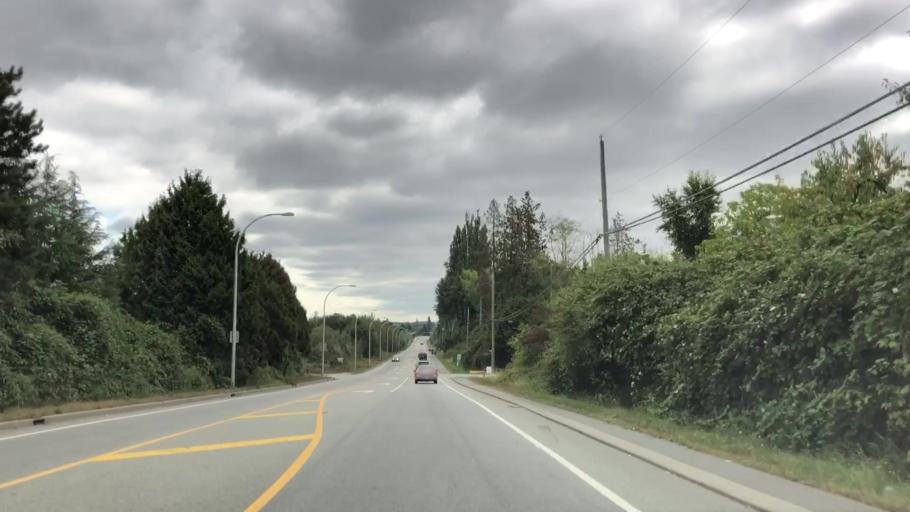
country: CA
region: British Columbia
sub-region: Greater Vancouver Regional District
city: White Rock
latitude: 49.0602
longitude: -122.7694
